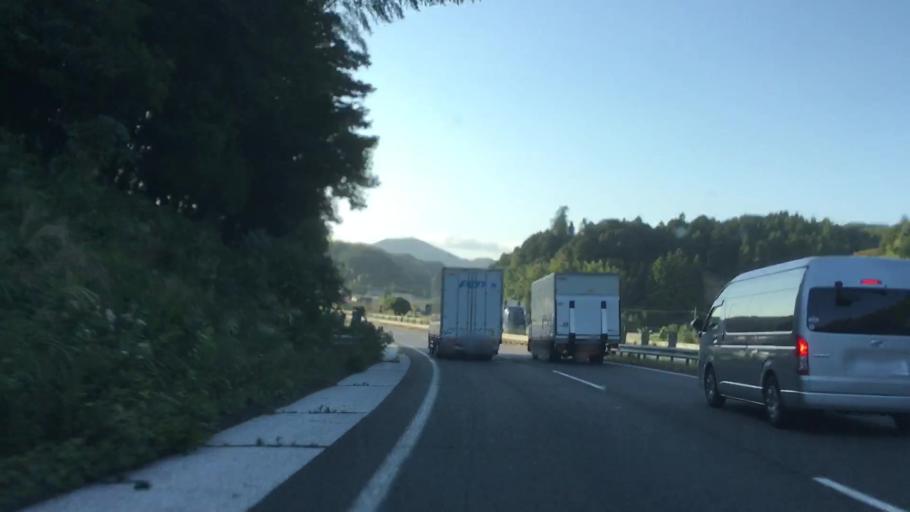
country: JP
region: Yamaguchi
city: Onoda
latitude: 34.1145
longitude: 131.1324
